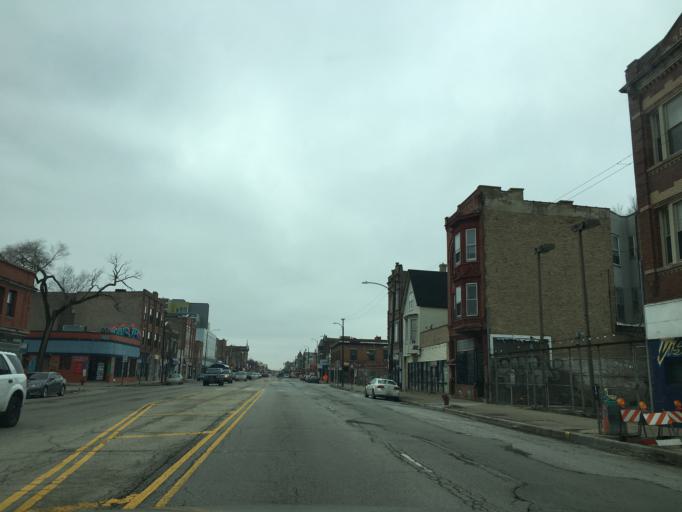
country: US
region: Illinois
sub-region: Cook County
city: Oak Park
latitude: 41.9101
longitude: -87.7137
